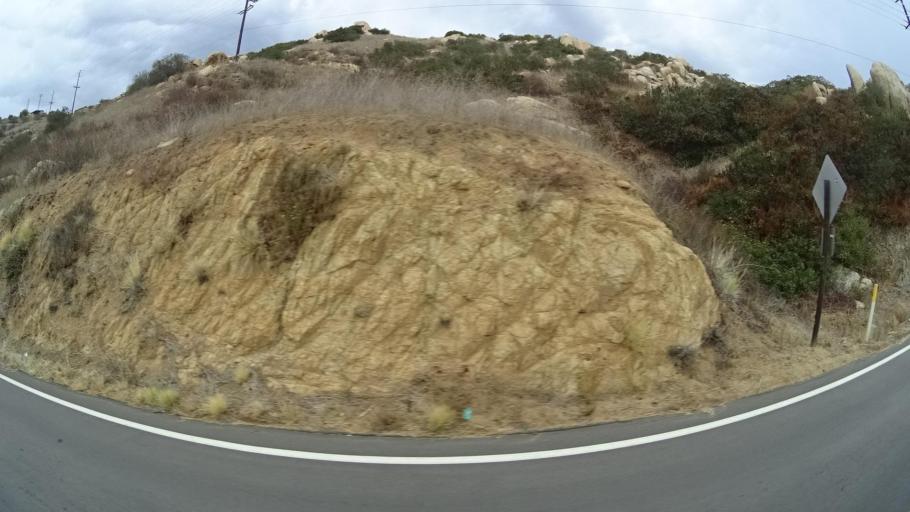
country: US
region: California
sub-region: San Diego County
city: San Pasqual
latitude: 33.0632
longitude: -117.0261
